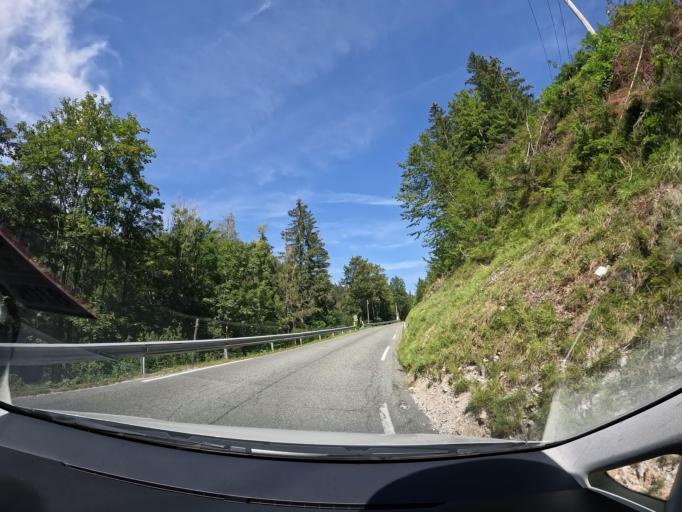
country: AT
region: Carinthia
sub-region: Politischer Bezirk Villach Land
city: Sankt Jakob
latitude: 46.5578
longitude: 14.0773
